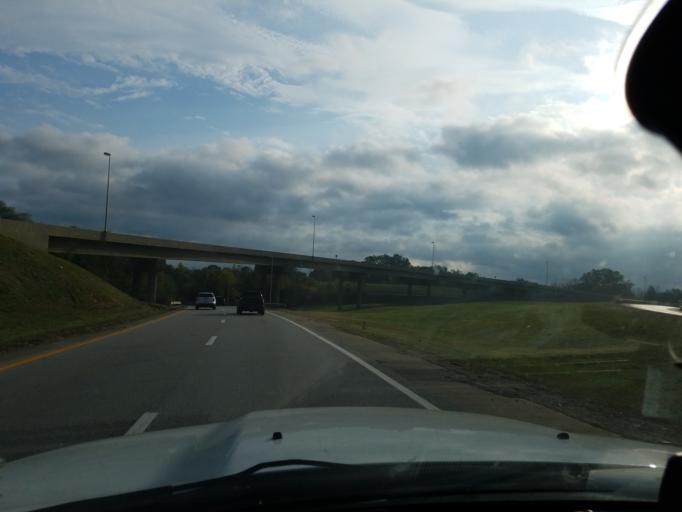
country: US
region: Indiana
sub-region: Floyd County
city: New Albany
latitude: 38.2753
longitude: -85.8115
